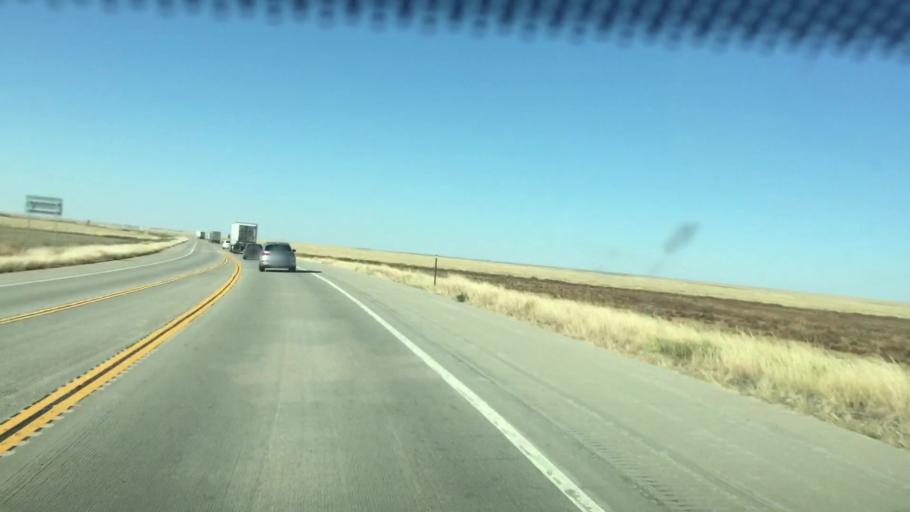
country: US
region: Colorado
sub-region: Kiowa County
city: Eads
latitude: 38.3508
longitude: -102.7143
